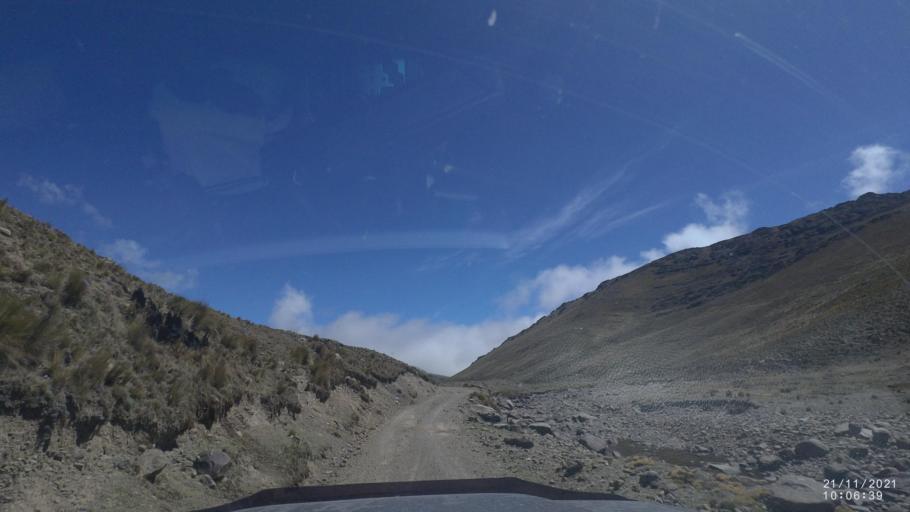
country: BO
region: Cochabamba
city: Cochabamba
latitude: -17.0129
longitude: -66.2849
